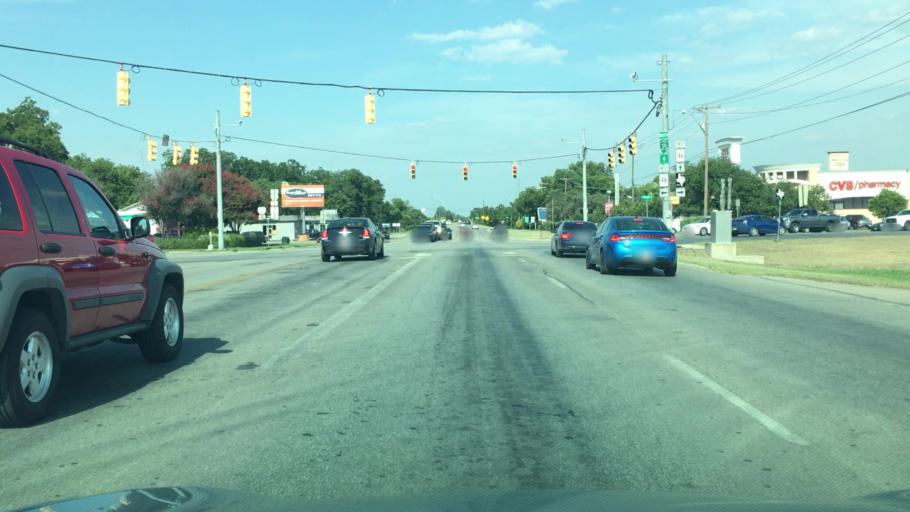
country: US
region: Texas
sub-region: Comal County
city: New Braunfels
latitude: 29.6937
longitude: -98.1117
